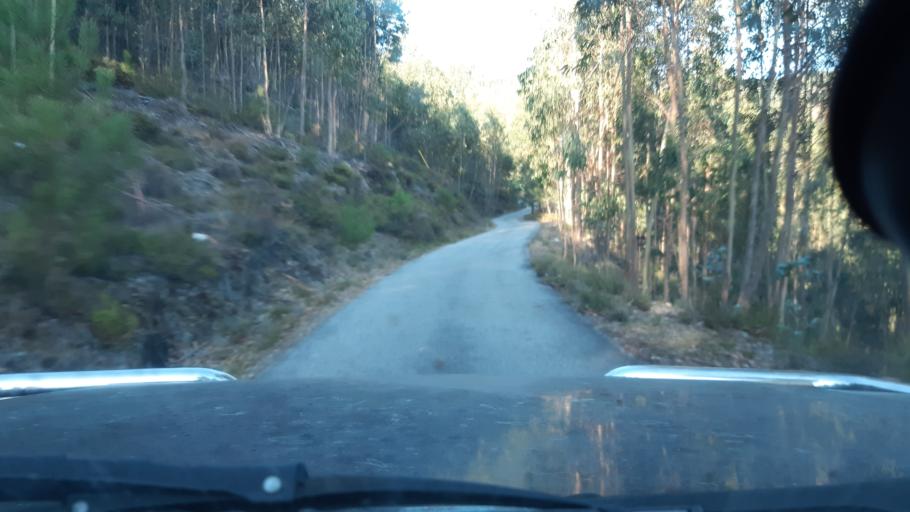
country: PT
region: Viseu
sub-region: Mortagua
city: Mortagua
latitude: 40.5325
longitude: -8.2485
